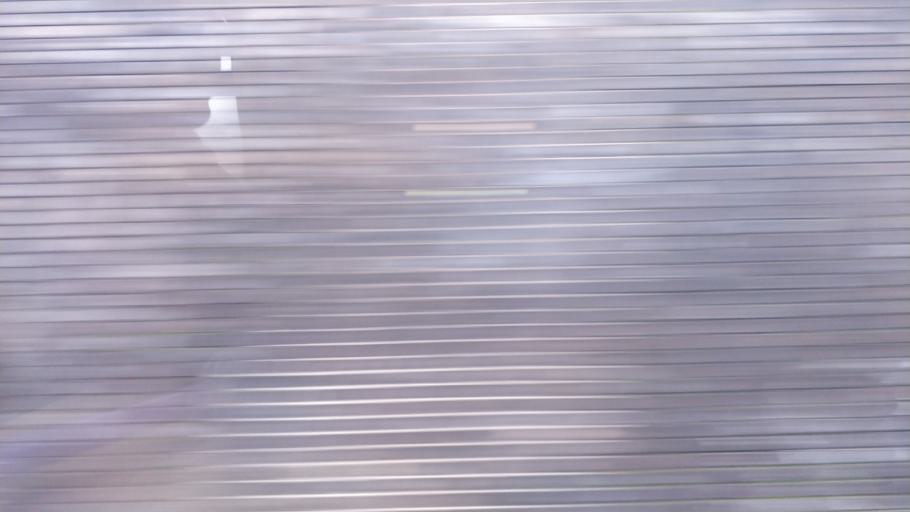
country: GB
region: England
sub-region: City and Borough of Salford
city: Salford
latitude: 53.4815
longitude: -2.2679
